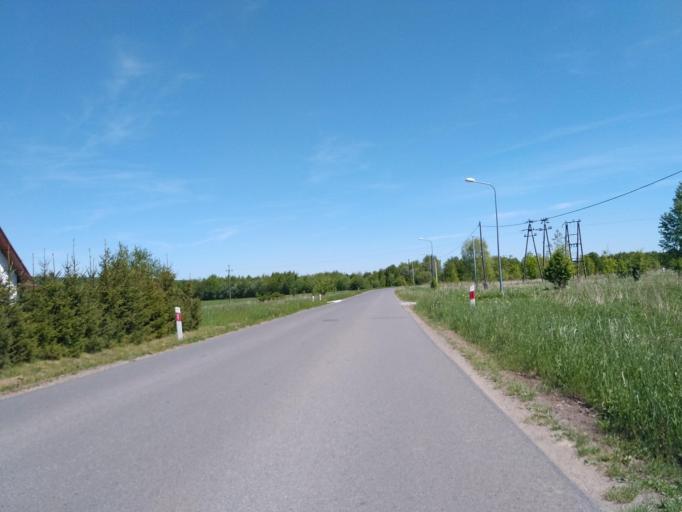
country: PL
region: Subcarpathian Voivodeship
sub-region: Powiat sanocki
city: Nowosielce-Gniewosz
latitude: 49.5517
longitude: 22.0861
